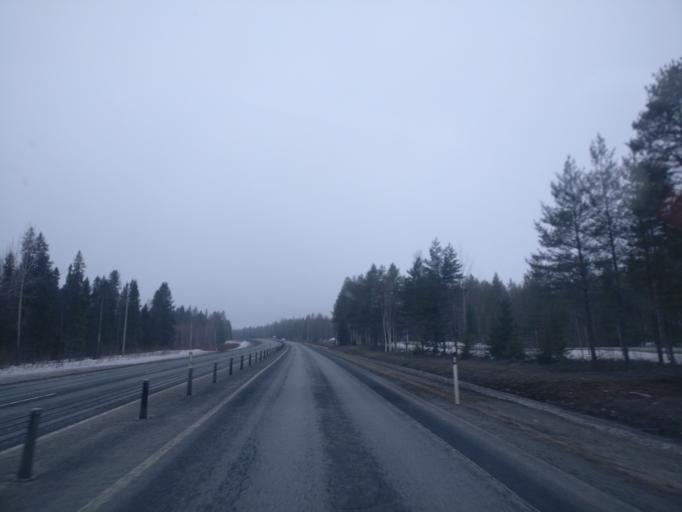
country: FI
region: Lapland
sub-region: Kemi-Tornio
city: Simo
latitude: 65.6678
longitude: 24.9714
